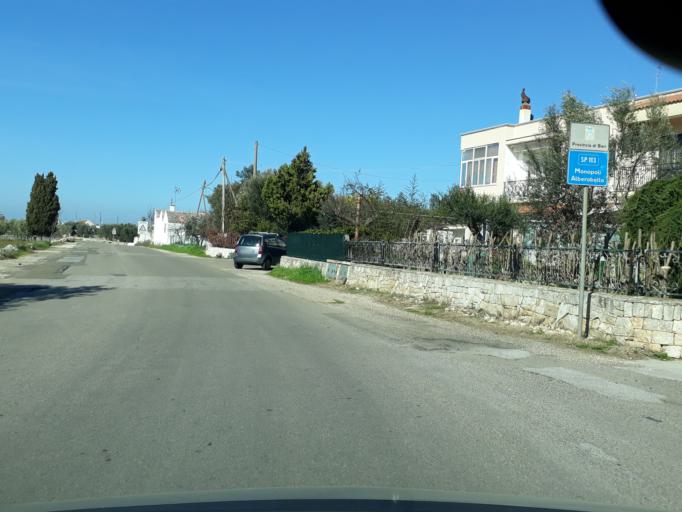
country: IT
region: Apulia
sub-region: Provincia di Bari
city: Alberobello
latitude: 40.7930
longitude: 17.2460
